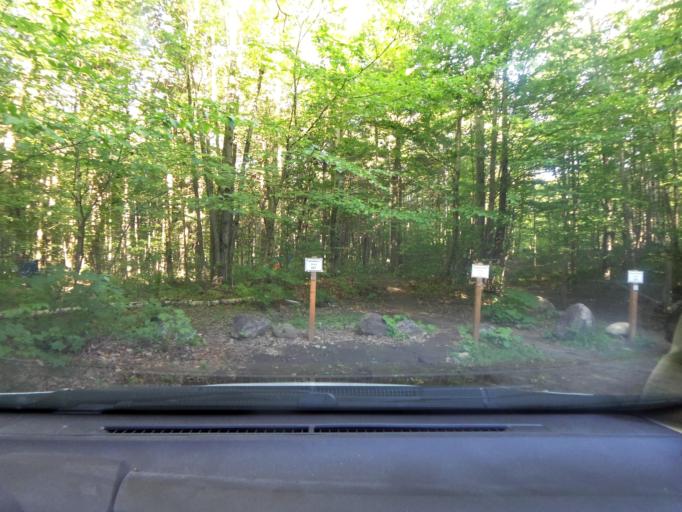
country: CA
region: Quebec
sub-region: Mauricie
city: Becancour
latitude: 46.5455
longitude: -72.4078
